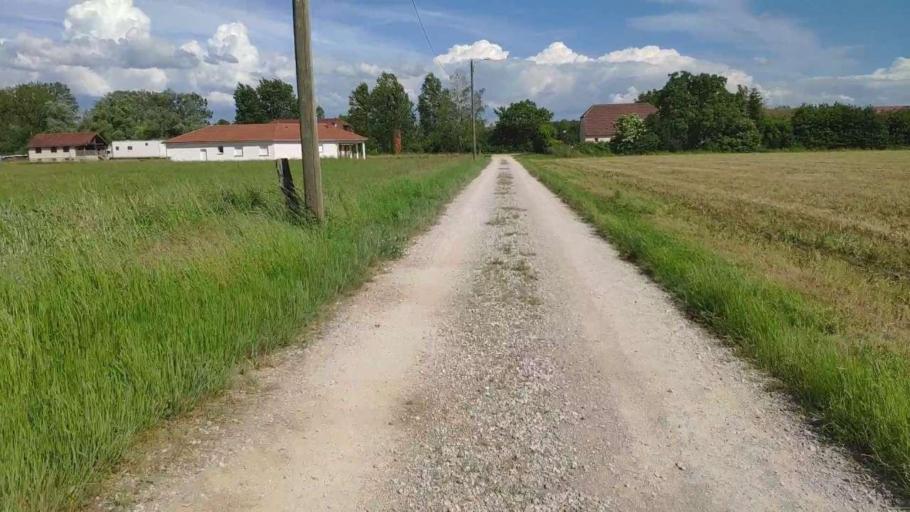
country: FR
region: Franche-Comte
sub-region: Departement du Jura
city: Bletterans
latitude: 46.7627
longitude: 5.4772
